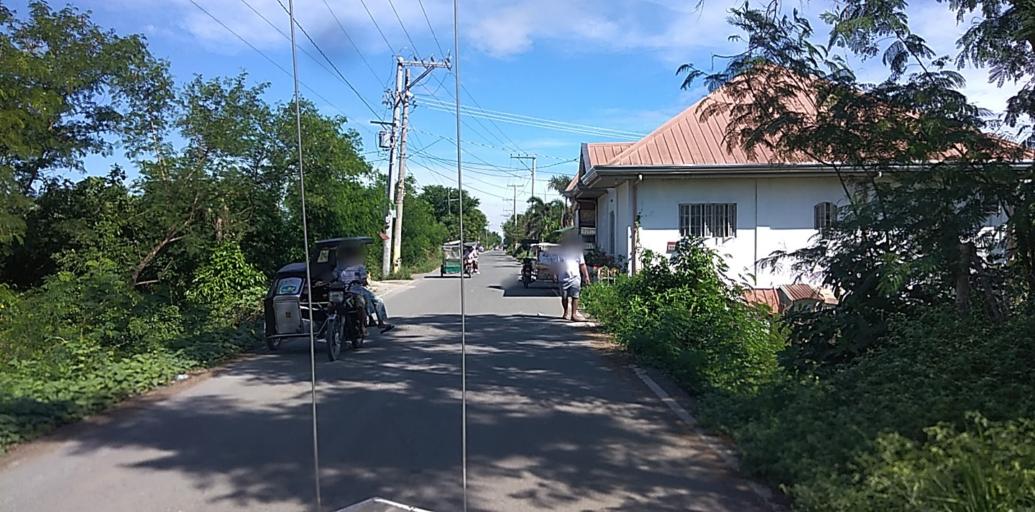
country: PH
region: Central Luzon
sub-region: Province of Pampanga
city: Candaba
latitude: 15.0832
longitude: 120.8095
